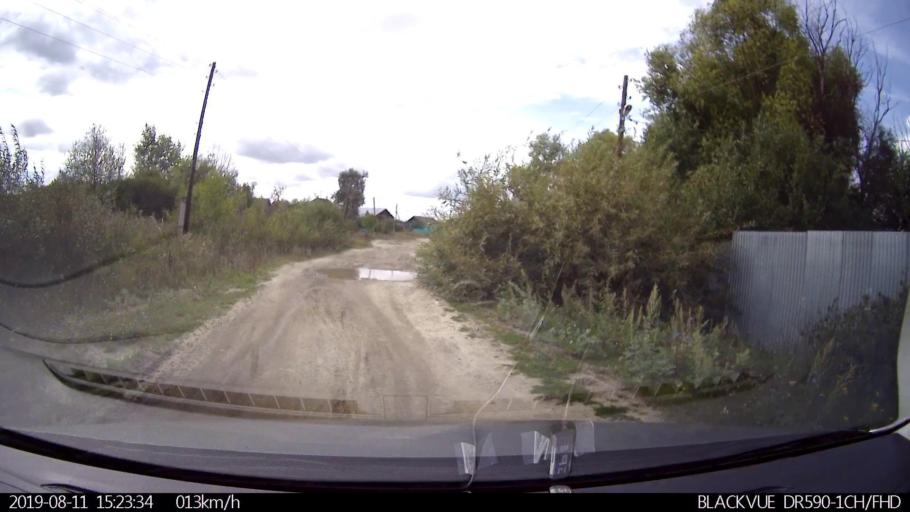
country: RU
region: Ulyanovsk
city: Ignatovka
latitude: 53.8481
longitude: 47.5801
